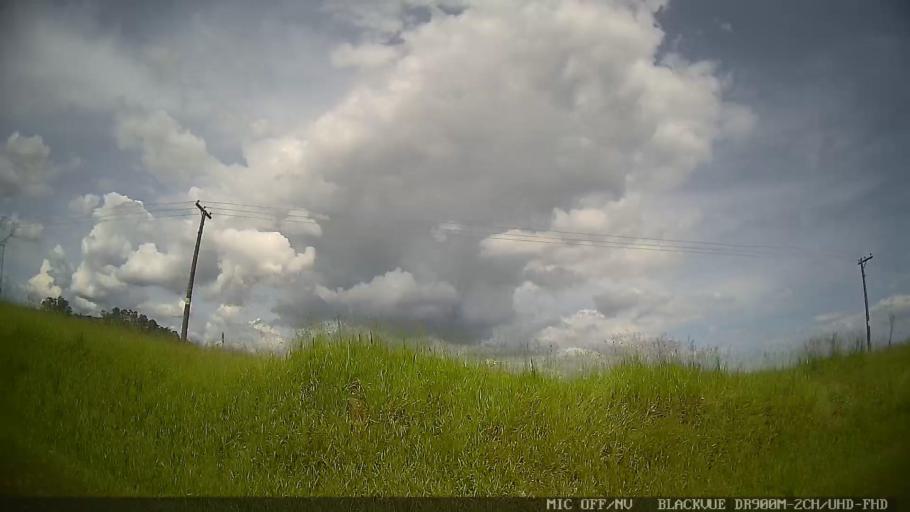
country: BR
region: Sao Paulo
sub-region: Mogi das Cruzes
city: Mogi das Cruzes
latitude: -23.6292
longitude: -46.2041
